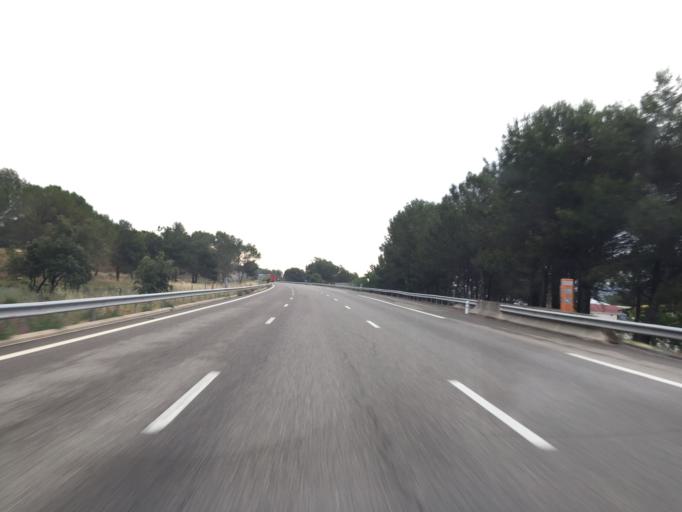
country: FR
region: Provence-Alpes-Cote d'Azur
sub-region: Departement du Var
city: La Celle
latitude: 43.4223
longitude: 5.9888
